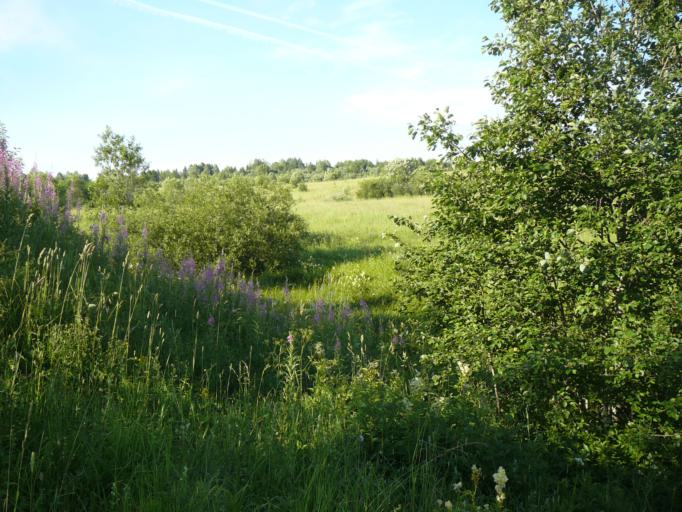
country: RU
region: Vologda
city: Ust'ye
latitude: 60.1466
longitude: 39.5687
